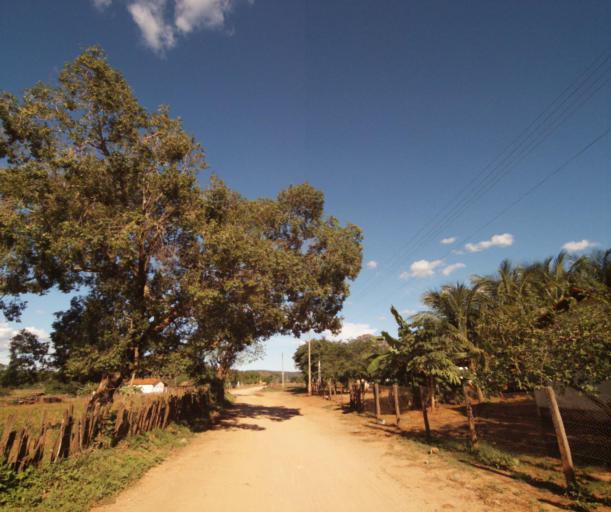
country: BR
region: Bahia
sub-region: Carinhanha
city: Carinhanha
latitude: -14.2747
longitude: -44.5105
